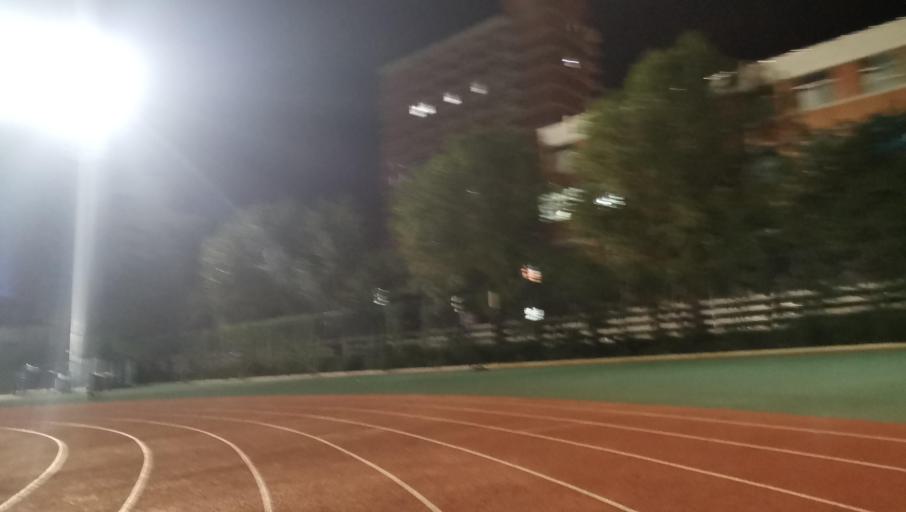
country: CN
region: Shandong Sheng
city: Jinan
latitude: 36.6498
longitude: 117.0125
